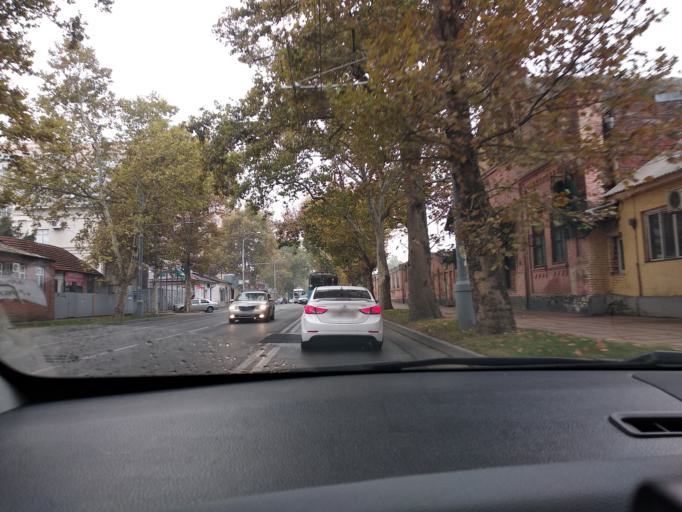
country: RU
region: Krasnodarskiy
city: Krasnodar
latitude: 45.0157
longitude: 38.9881
